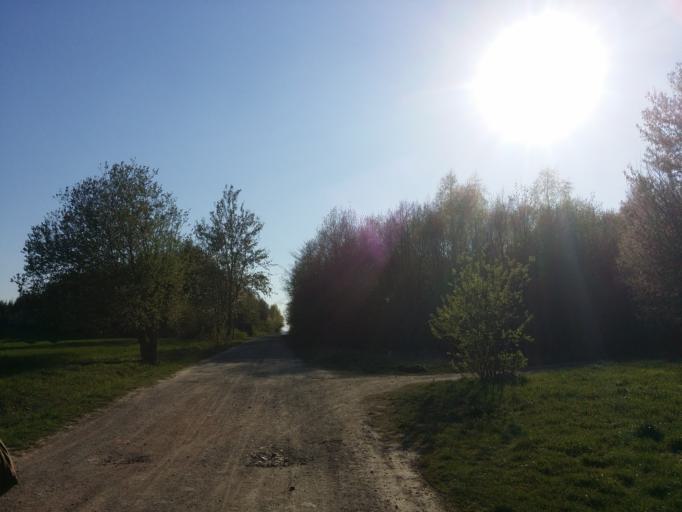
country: DE
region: Saxony
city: Burkhardtsdorf
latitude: 50.7747
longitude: 12.9589
